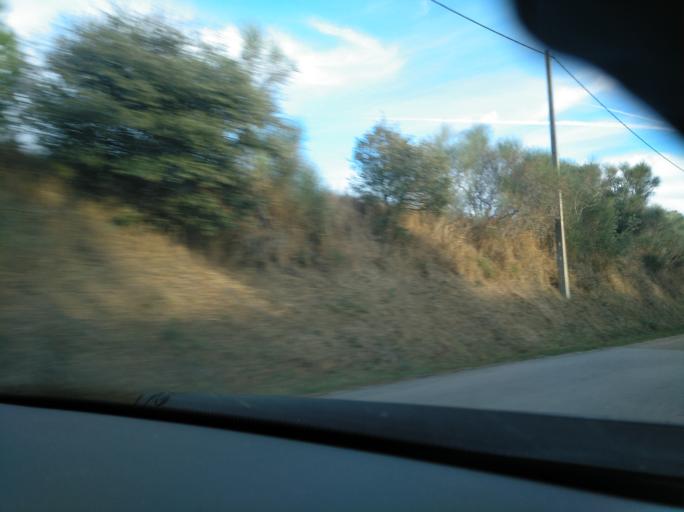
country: PT
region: Evora
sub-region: Arraiolos
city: Arraiolos
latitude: 38.8442
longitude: -7.8293
